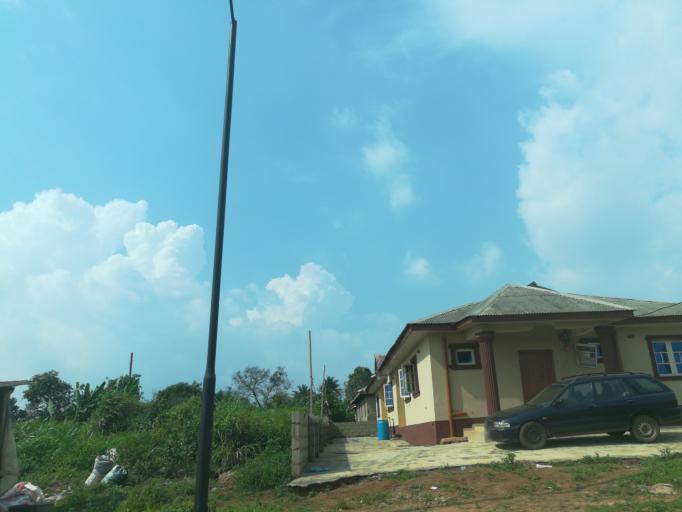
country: NG
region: Lagos
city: Ikorodu
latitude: 6.6403
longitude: 3.6685
